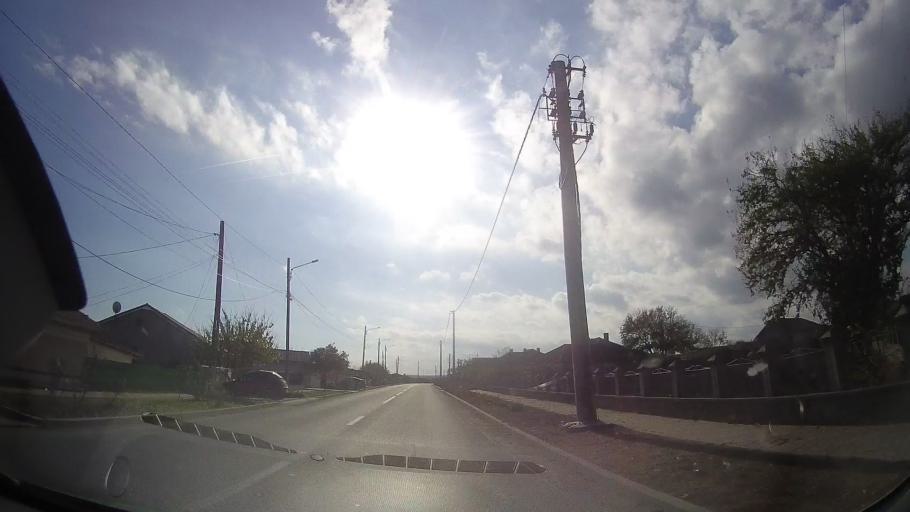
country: RO
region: Constanta
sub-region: Comuna Douazeci si Trei August
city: Dulcesti
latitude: 43.9098
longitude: 28.5497
